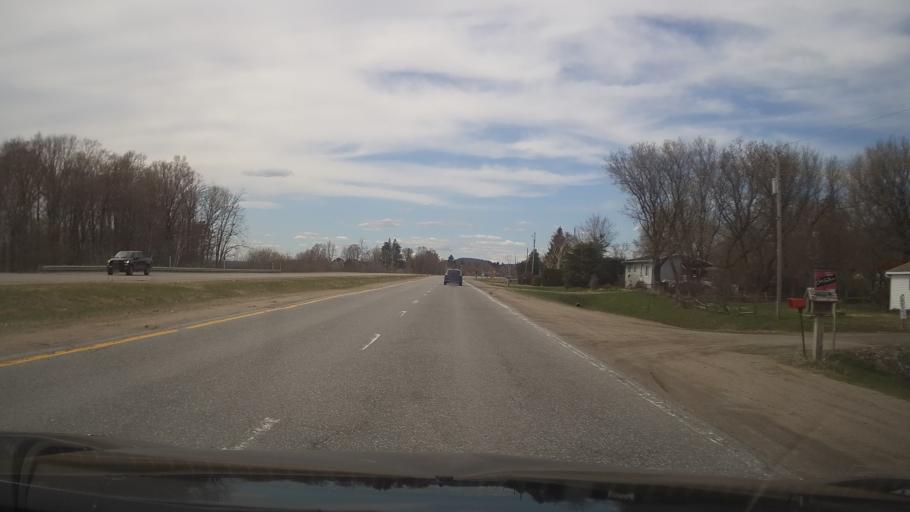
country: CA
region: Quebec
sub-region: Outaouais
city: Wakefield
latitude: 45.5257
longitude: -75.9968
